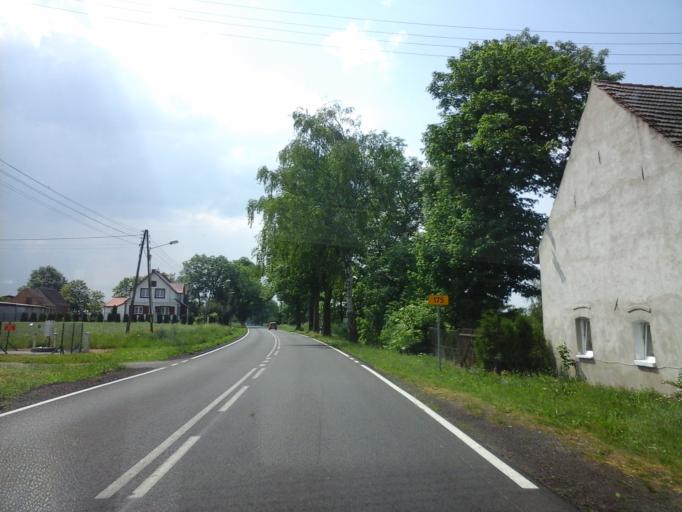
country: PL
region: West Pomeranian Voivodeship
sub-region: Powiat choszczenski
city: Recz
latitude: 53.1891
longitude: 15.5821
